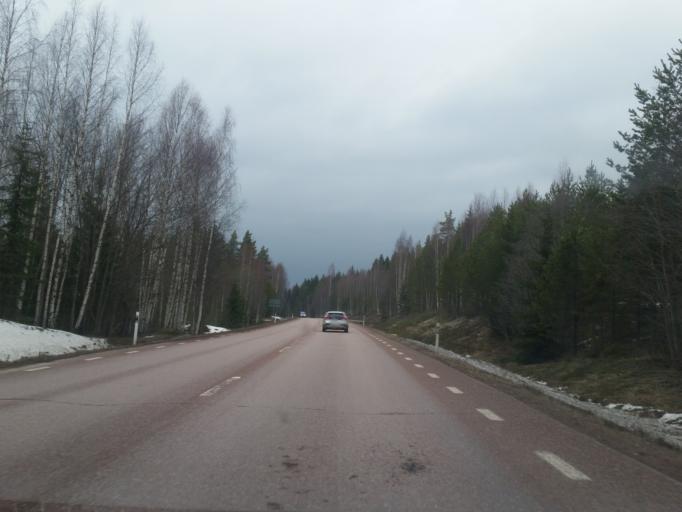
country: SE
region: Dalarna
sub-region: Alvdalens Kommun
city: AElvdalen
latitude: 61.1144
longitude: 14.2623
